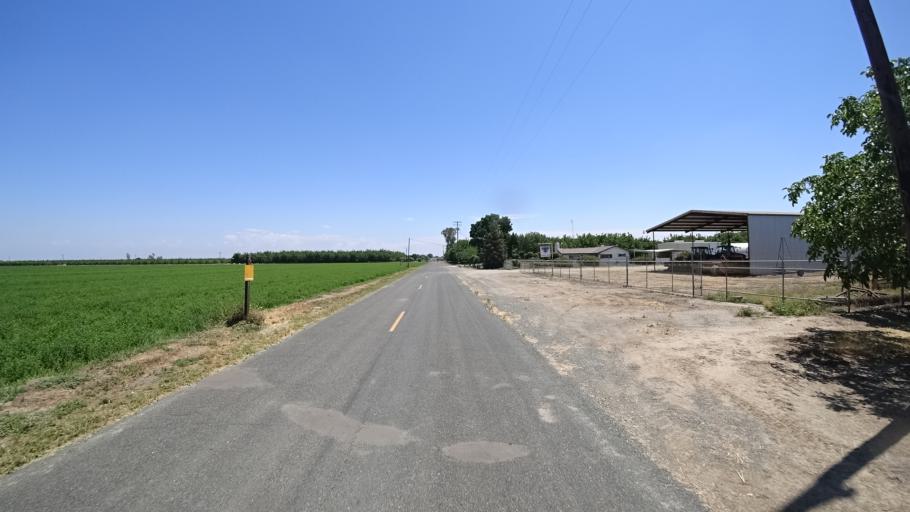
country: US
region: California
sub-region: Fresno County
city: Laton
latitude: 36.4379
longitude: -119.6043
